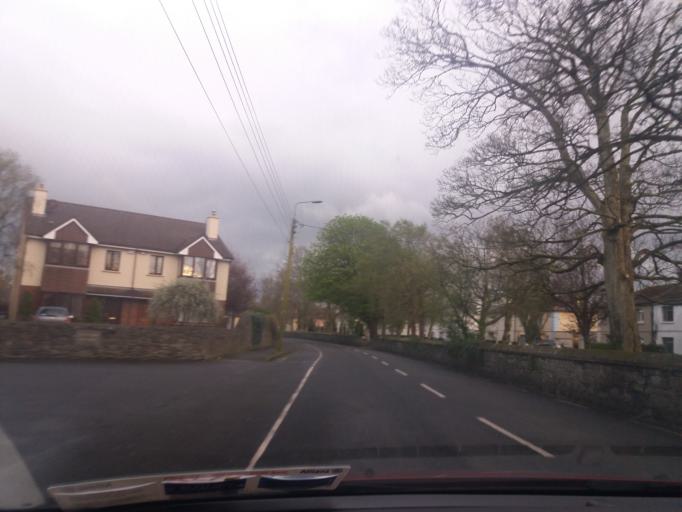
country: IE
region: Munster
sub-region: Ciarrai
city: Tralee
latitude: 52.2649
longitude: -9.6975
